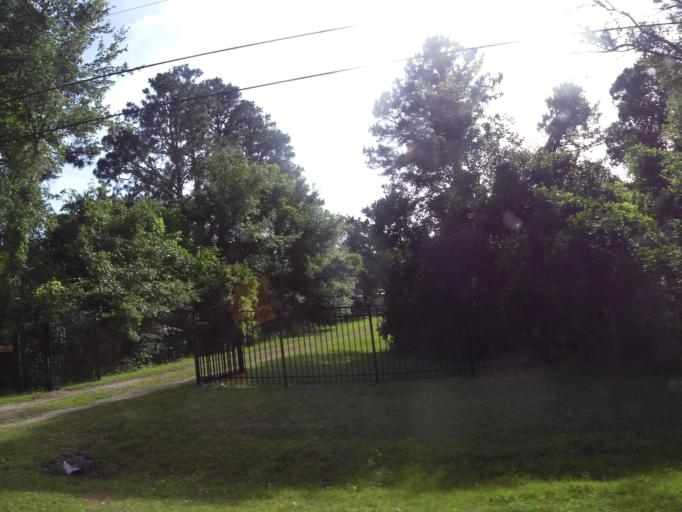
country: US
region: Florida
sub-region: Nassau County
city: Fernandina Beach
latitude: 30.5315
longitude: -81.4885
